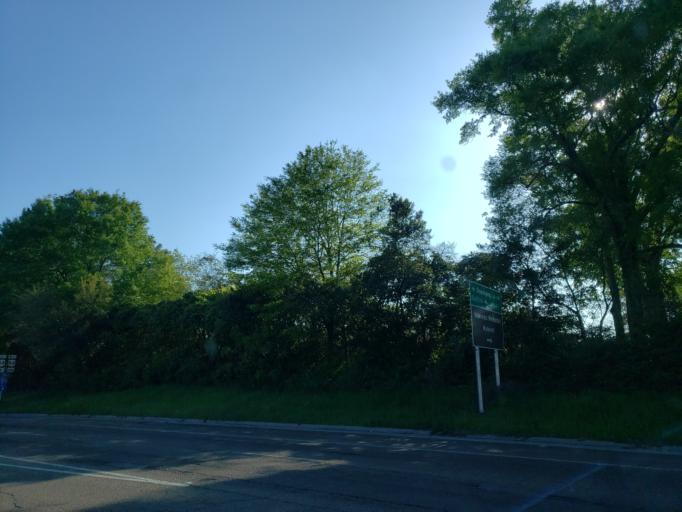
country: US
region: Mississippi
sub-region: Jones County
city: Laurel
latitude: 31.6957
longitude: -89.1468
